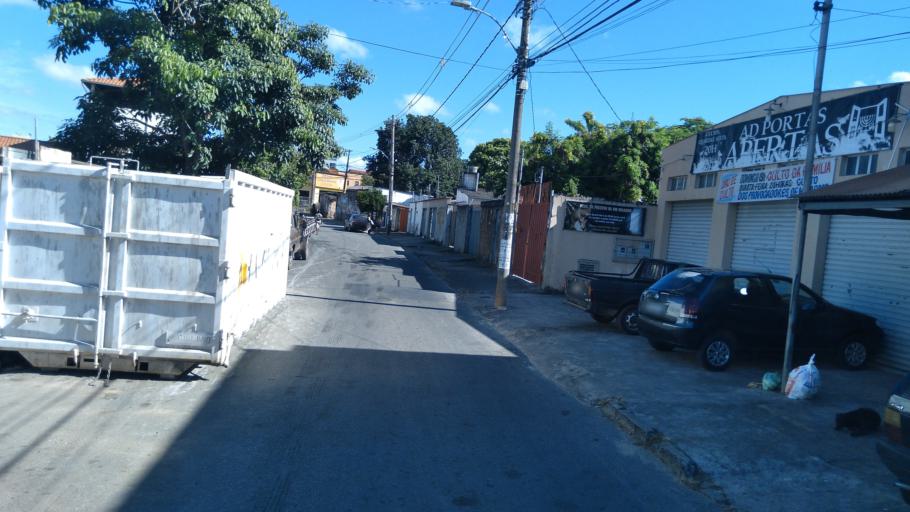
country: BR
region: Minas Gerais
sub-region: Belo Horizonte
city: Belo Horizonte
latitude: -19.8539
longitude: -43.9119
